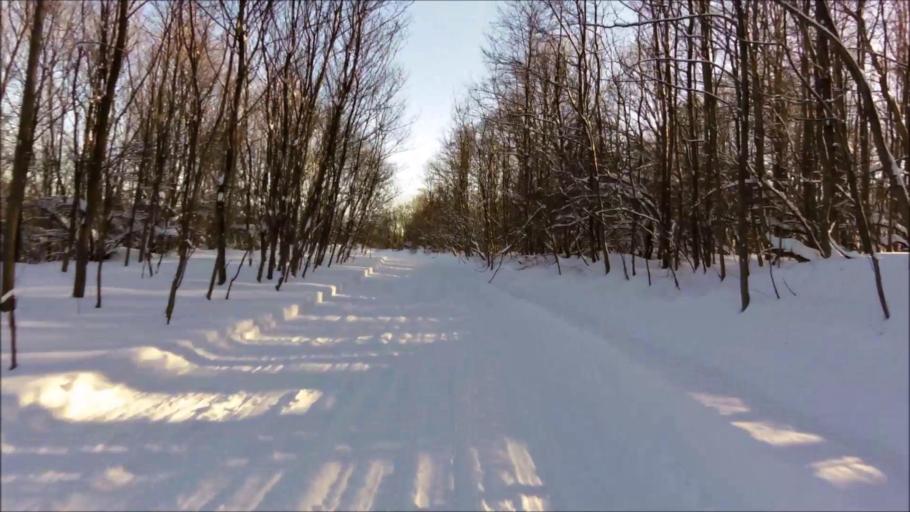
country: US
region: New York
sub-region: Chautauqua County
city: Mayville
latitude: 42.2533
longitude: -79.3867
